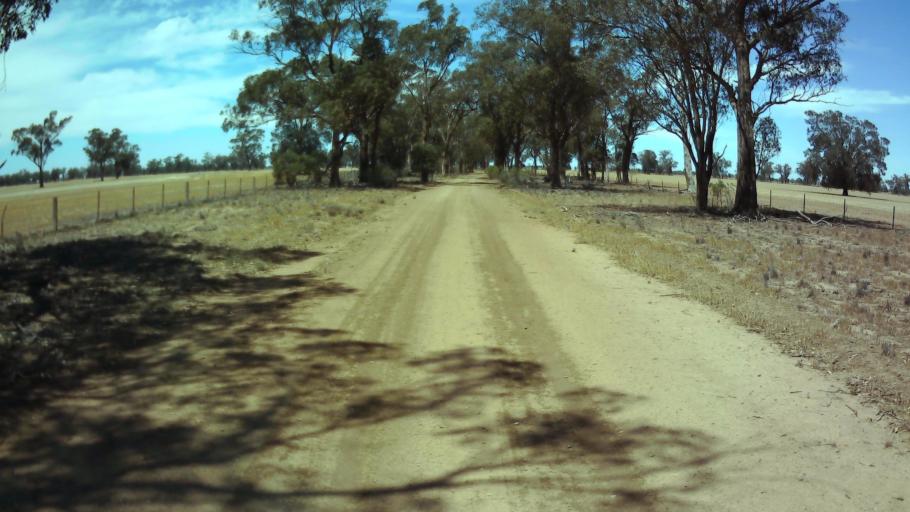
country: AU
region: New South Wales
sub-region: Weddin
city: Grenfell
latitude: -33.9267
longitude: 147.8037
